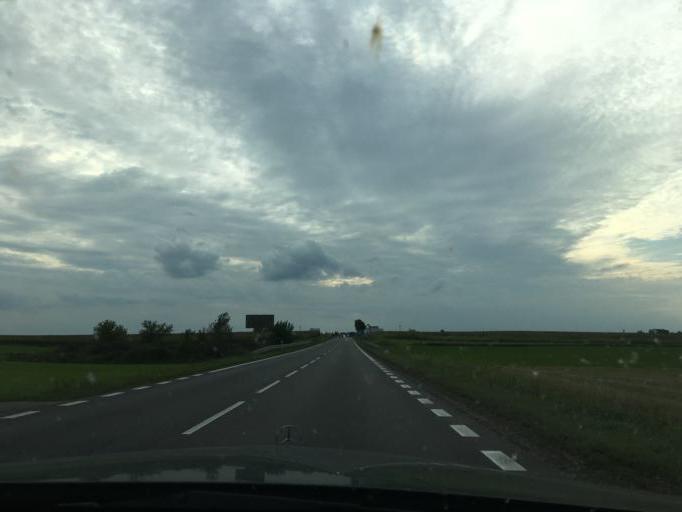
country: PL
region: Podlasie
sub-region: Powiat grajewski
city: Grajewo
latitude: 53.6375
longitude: 22.4336
